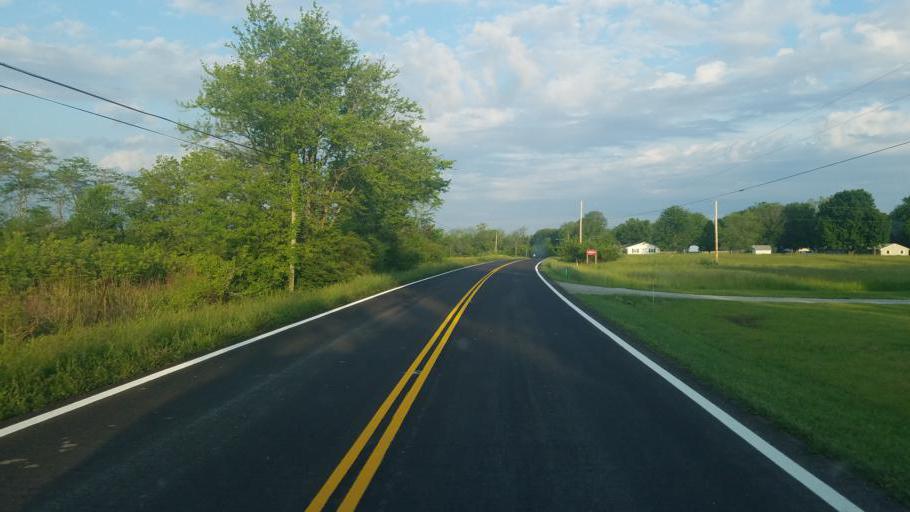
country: US
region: Ohio
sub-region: Highland County
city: Leesburg
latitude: 39.3549
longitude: -83.5384
